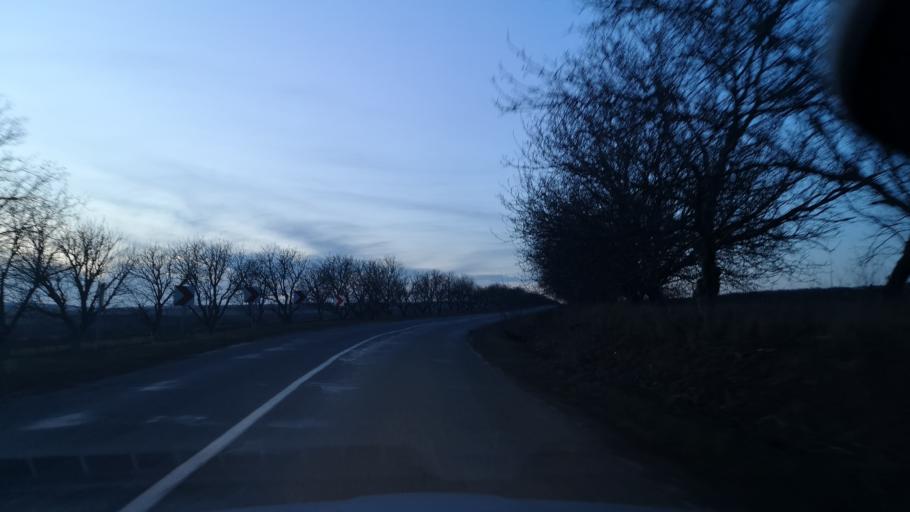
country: MD
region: Orhei
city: Orhei
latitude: 47.2854
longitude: 28.8267
